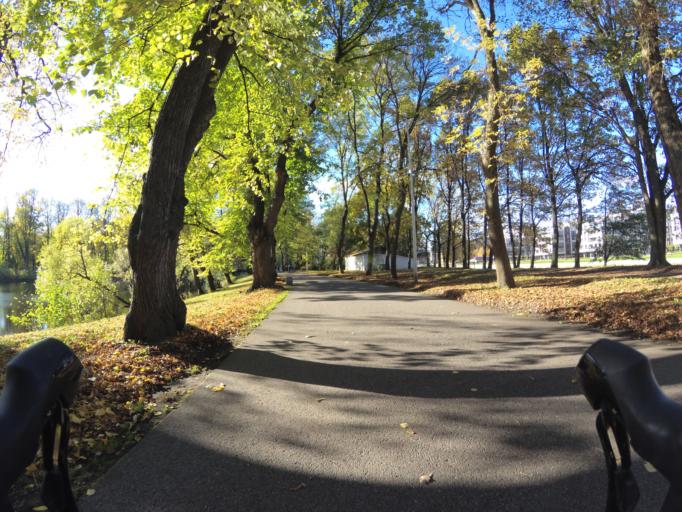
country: RU
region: St.-Petersburg
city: Staraya Derevnya
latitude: 59.9816
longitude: 30.2478
